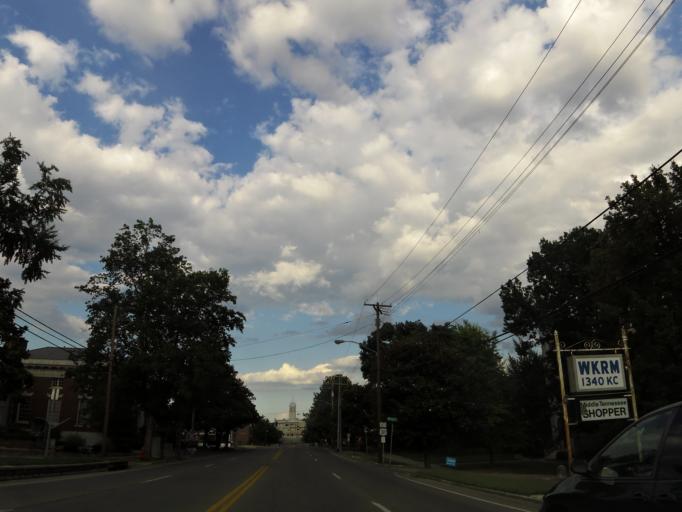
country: US
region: Tennessee
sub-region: Maury County
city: Columbia
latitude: 35.6154
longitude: -87.0391
